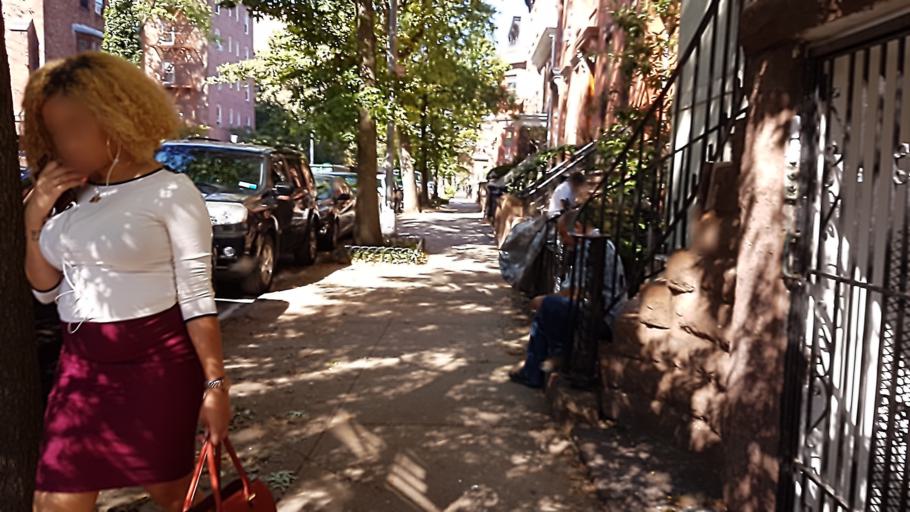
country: US
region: New York
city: New York City
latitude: 40.6879
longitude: -73.9936
